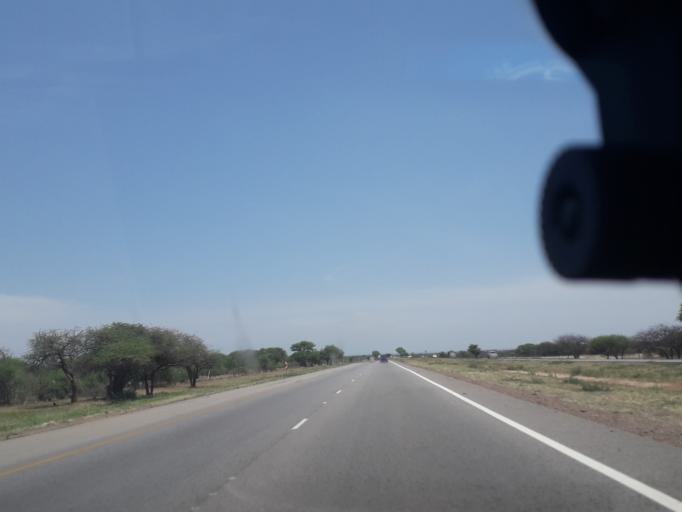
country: ZA
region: North-West
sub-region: Bojanala Platinum District Municipality
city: Makapanstad
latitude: -25.1688
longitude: 28.3072
